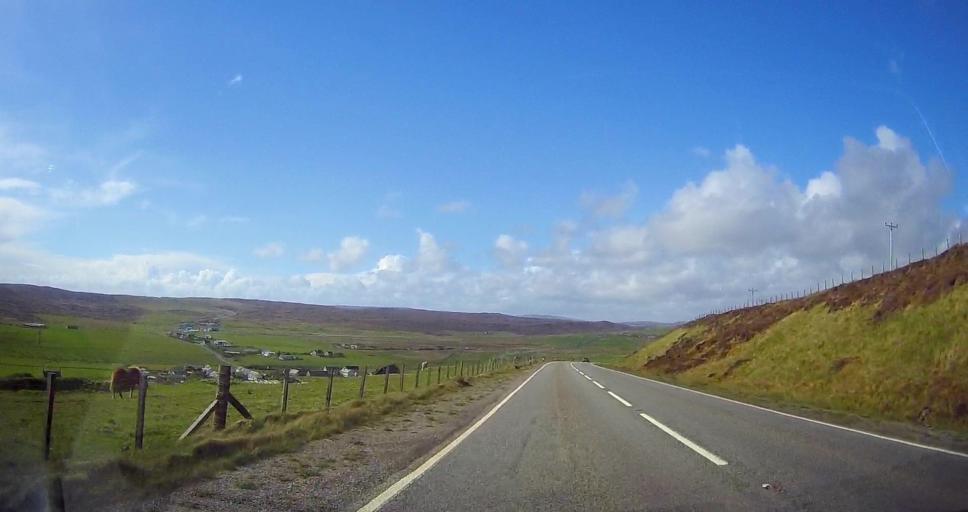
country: GB
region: Scotland
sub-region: Shetland Islands
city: Lerwick
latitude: 60.1784
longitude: -1.2240
